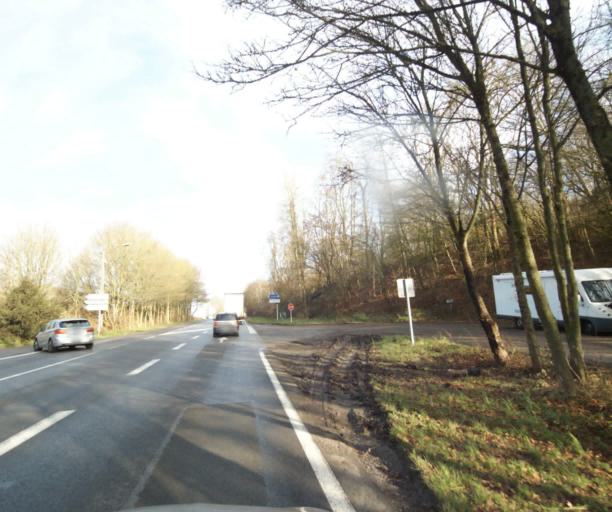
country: FR
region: Nord-Pas-de-Calais
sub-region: Departement du Nord
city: Famars
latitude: 50.3245
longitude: 3.5061
